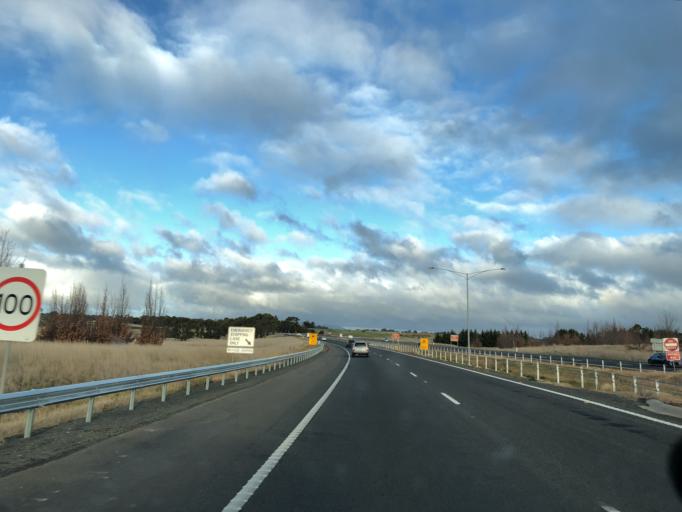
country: AU
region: Victoria
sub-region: Mount Alexander
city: Castlemaine
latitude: -37.2198
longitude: 144.4166
